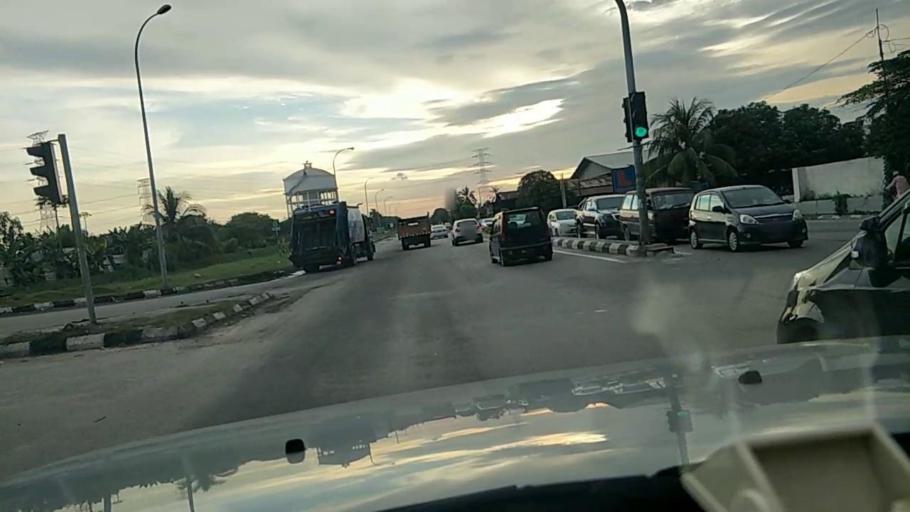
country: MY
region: Selangor
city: Klang
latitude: 3.1123
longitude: 101.4370
